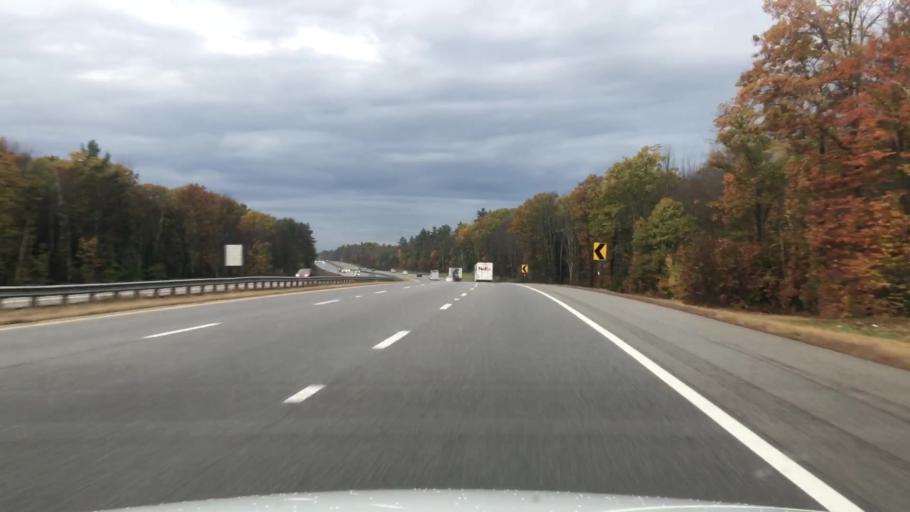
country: US
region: Maine
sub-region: York County
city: Biddeford
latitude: 43.4632
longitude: -70.5225
